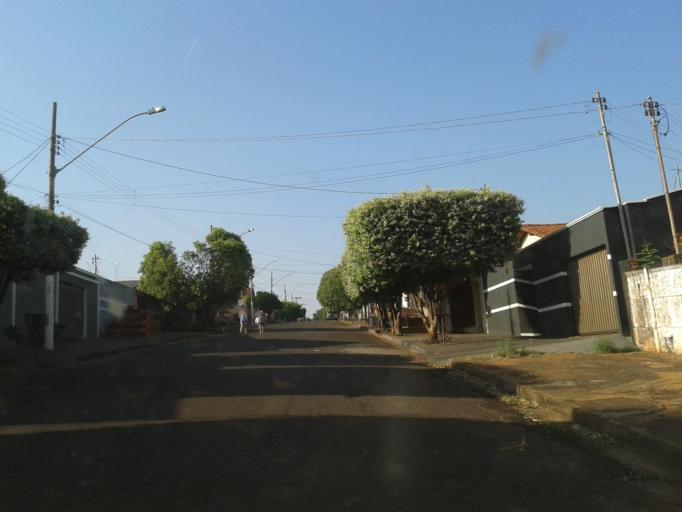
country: BR
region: Minas Gerais
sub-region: Ituiutaba
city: Ituiutaba
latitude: -18.9621
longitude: -49.4708
